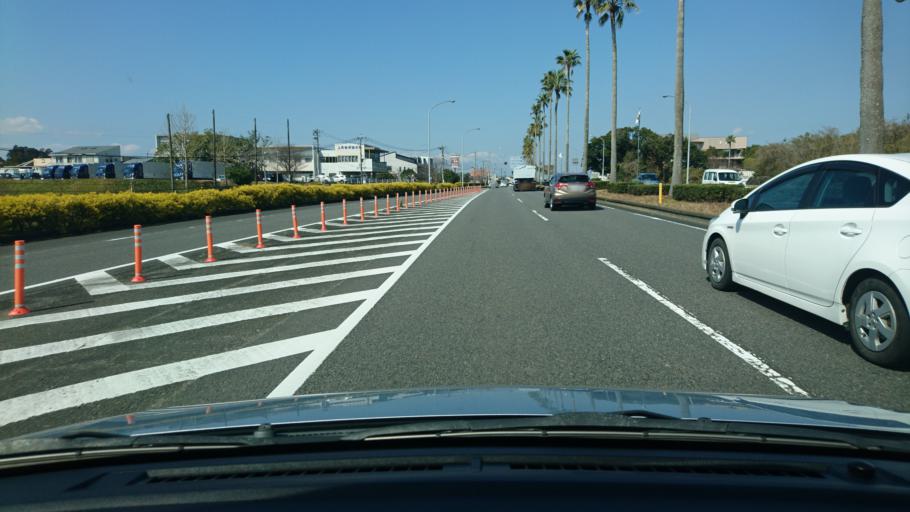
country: JP
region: Miyazaki
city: Miyazaki-shi
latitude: 31.8730
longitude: 131.4136
